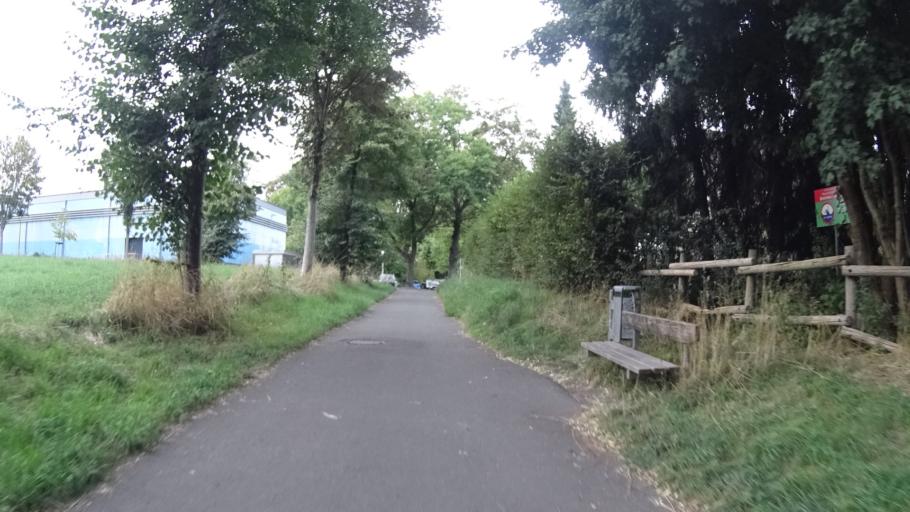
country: DE
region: North Rhine-Westphalia
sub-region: Regierungsbezirk Arnsberg
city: Dortmund
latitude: 51.4896
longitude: 7.4290
